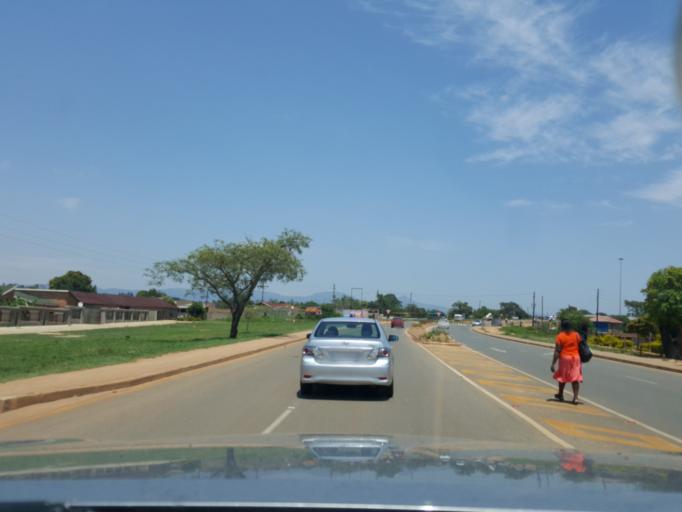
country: ZA
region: Limpopo
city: Thulamahashi
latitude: -24.8426
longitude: 31.0804
